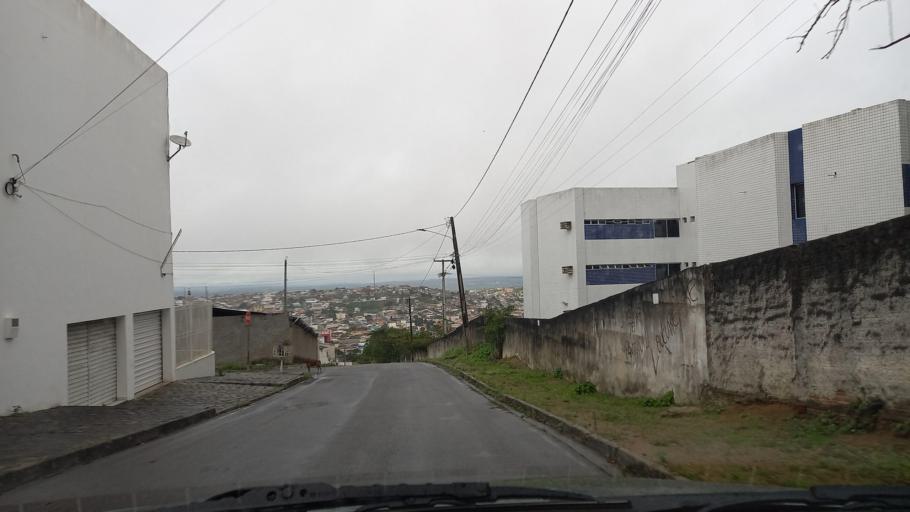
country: BR
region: Pernambuco
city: Garanhuns
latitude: -8.8842
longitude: -36.4961
